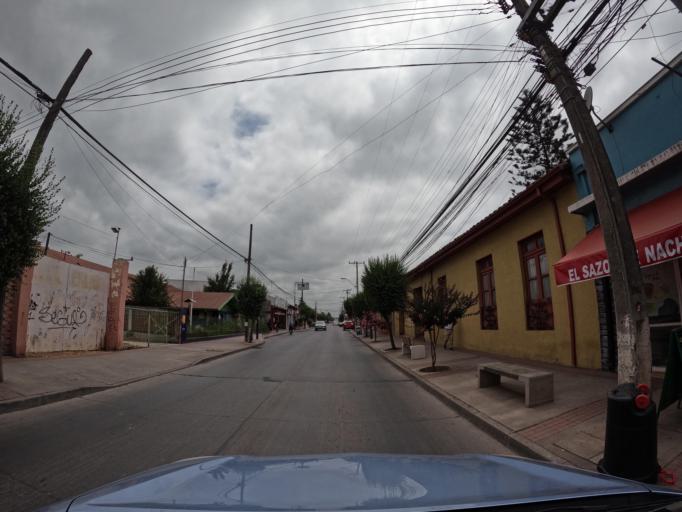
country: CL
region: O'Higgins
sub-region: Provincia de Colchagua
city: Chimbarongo
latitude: -34.7094
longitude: -71.0443
